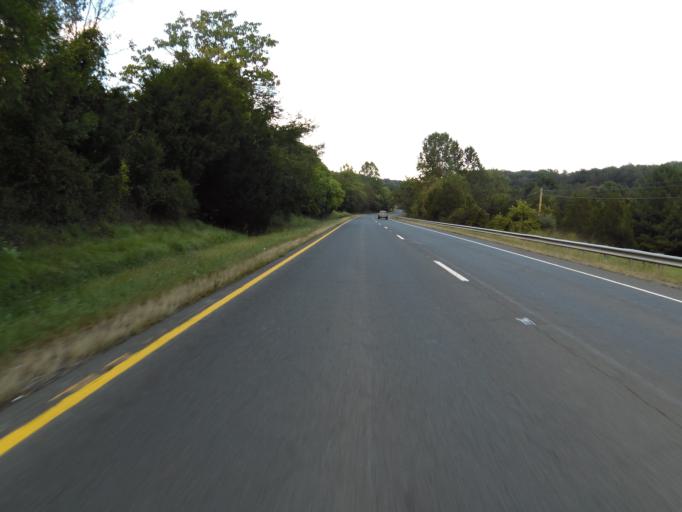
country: US
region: Virginia
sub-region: Fauquier County
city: Warrenton
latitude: 38.6964
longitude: -77.8893
